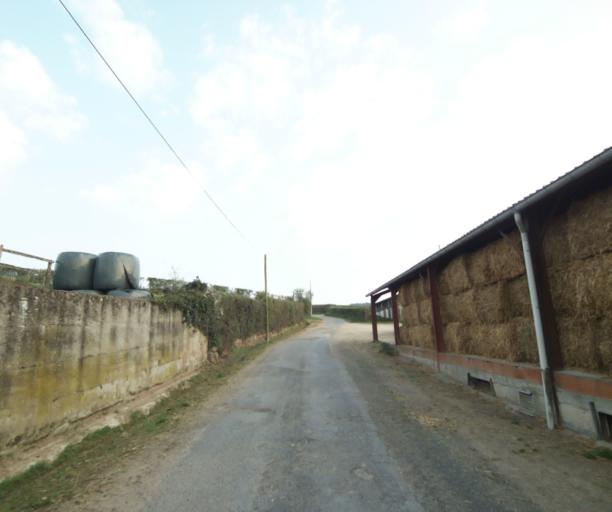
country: FR
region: Bourgogne
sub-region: Departement de Saone-et-Loire
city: Matour
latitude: 46.4281
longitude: 4.4637
